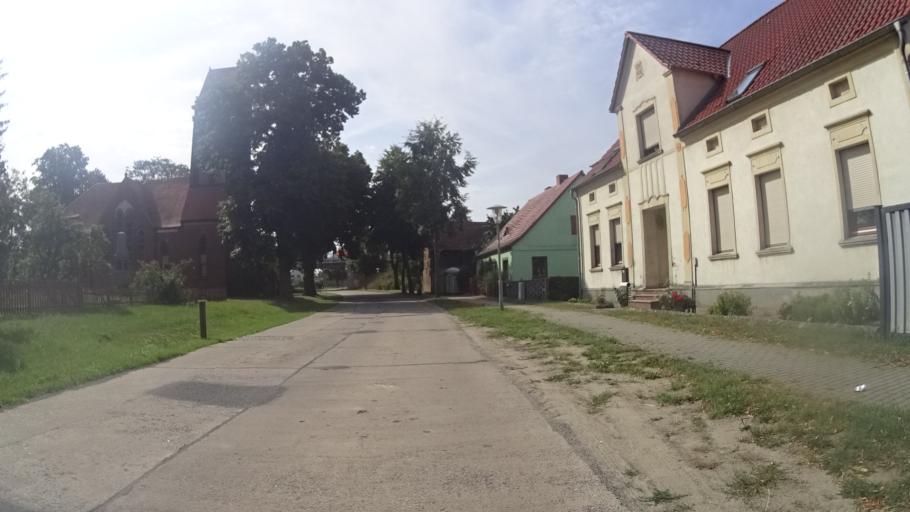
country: DE
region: Brandenburg
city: Golzow
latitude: 52.3366
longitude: 12.6611
